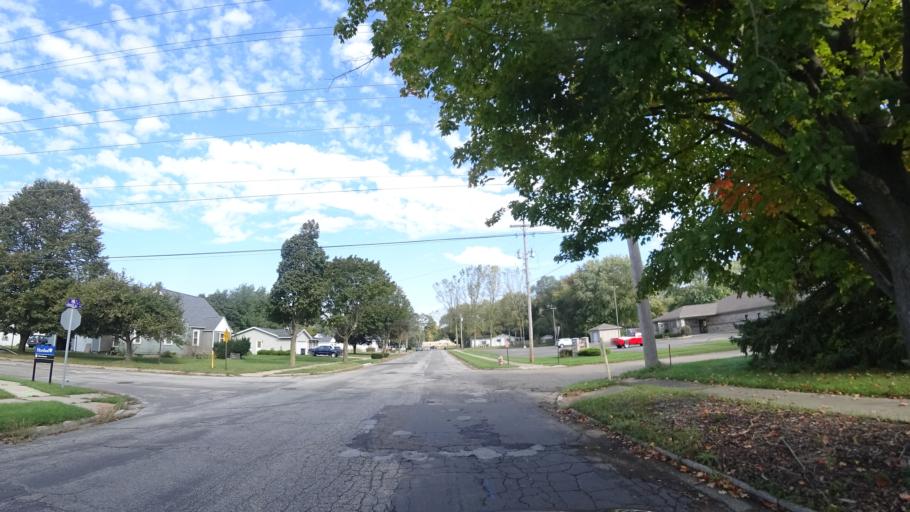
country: US
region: Michigan
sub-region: Saint Joseph County
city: Three Rivers
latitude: 41.9380
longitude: -85.6422
